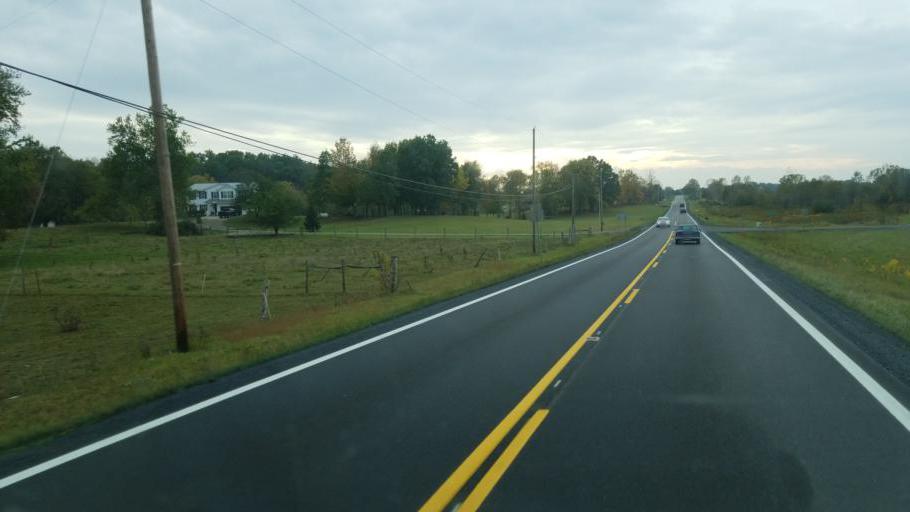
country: US
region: Ohio
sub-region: Knox County
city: Centerburg
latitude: 40.4037
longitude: -82.6376
